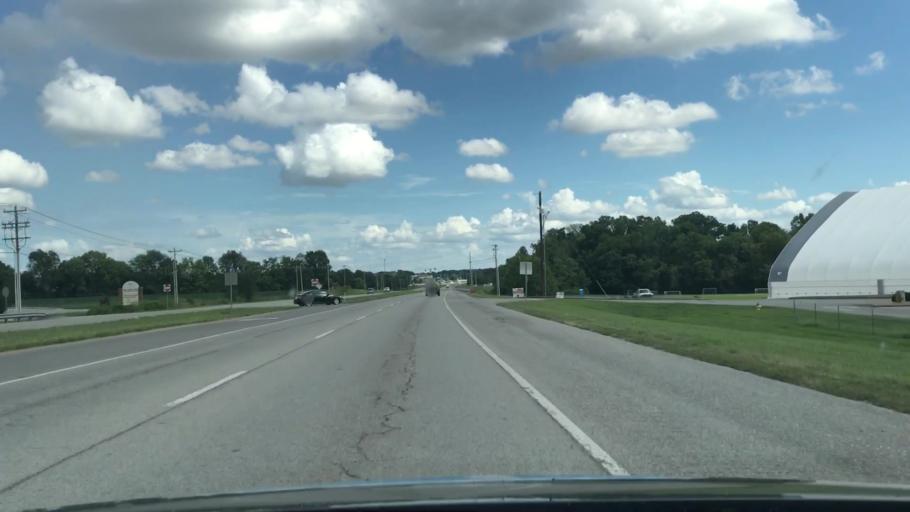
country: US
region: Kentucky
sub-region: Christian County
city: Hopkinsville
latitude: 36.8298
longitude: -87.5188
